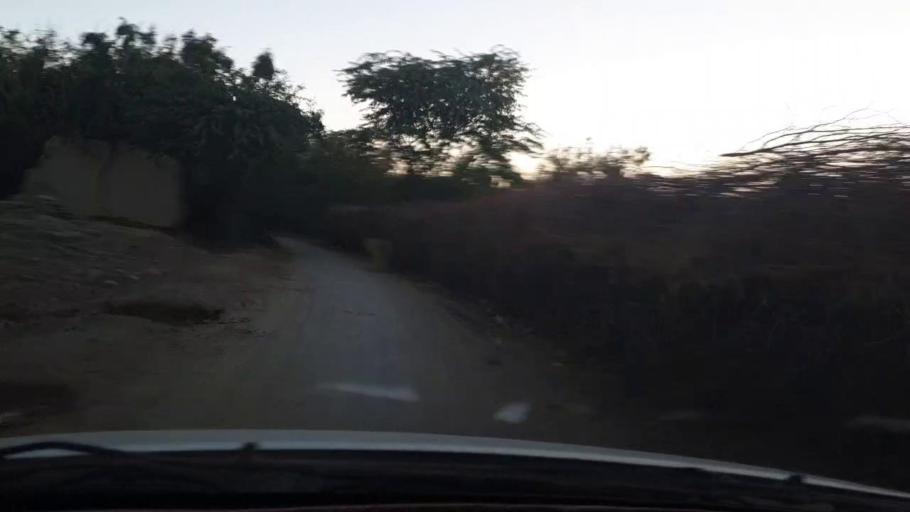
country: PK
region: Sindh
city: Johi
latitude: 26.8307
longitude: 67.4449
